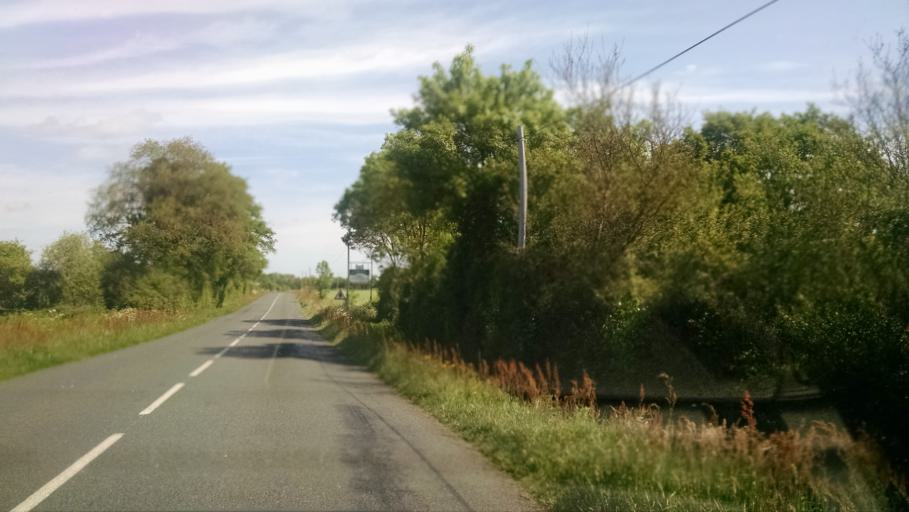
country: FR
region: Pays de la Loire
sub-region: Departement de la Vendee
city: Saint-Hilaire-de-Loulay
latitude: 47.0327
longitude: -1.3275
